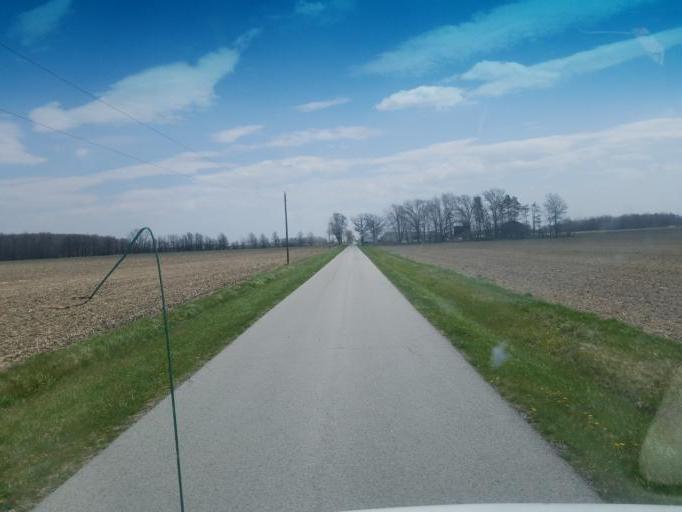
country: US
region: Ohio
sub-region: Hardin County
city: Forest
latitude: 40.7744
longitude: -83.4907
